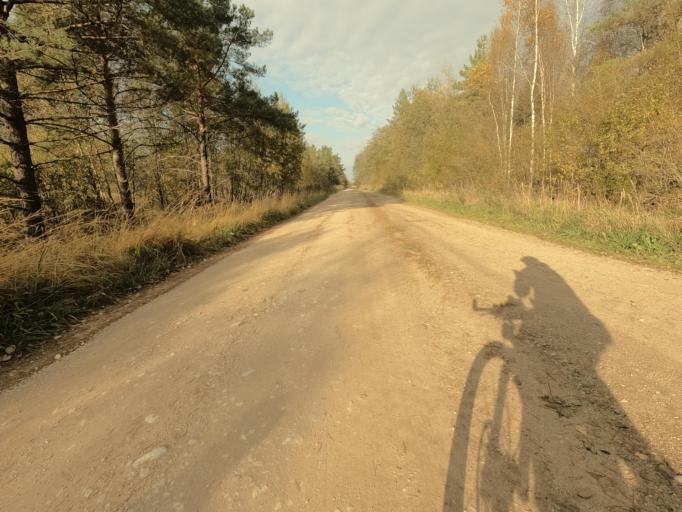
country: RU
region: Novgorod
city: Volkhovskiy
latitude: 58.8978
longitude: 31.0312
